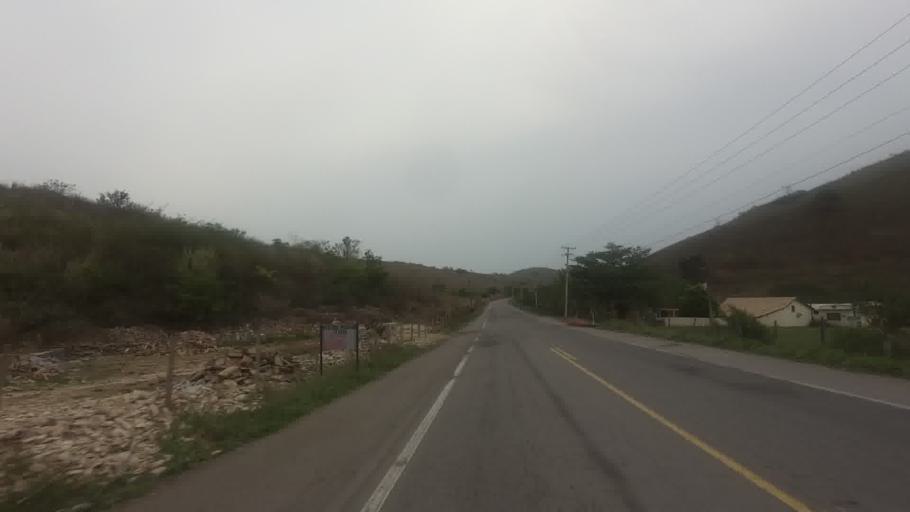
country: BR
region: Rio de Janeiro
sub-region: Santo Antonio De Padua
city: Santo Antonio de Padua
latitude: -21.5995
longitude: -42.2323
